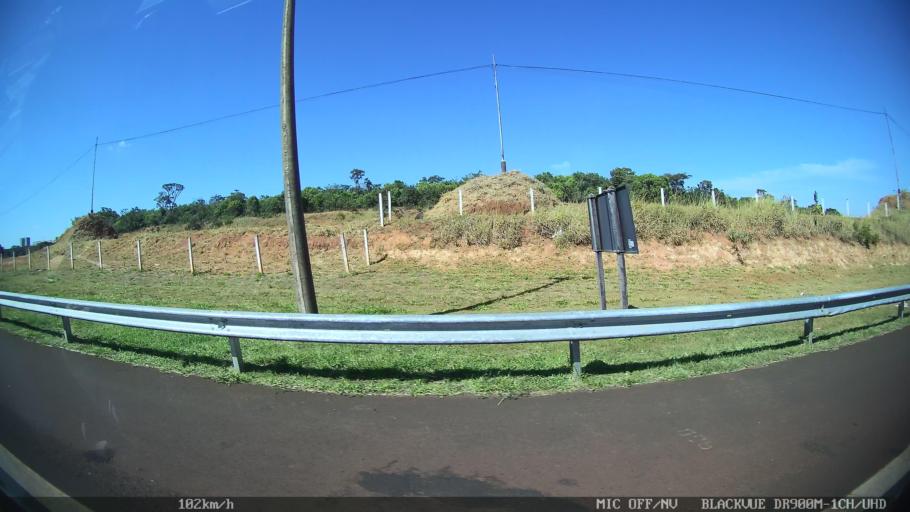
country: BR
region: Sao Paulo
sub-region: Franca
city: Franca
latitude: -20.5652
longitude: -47.4200
